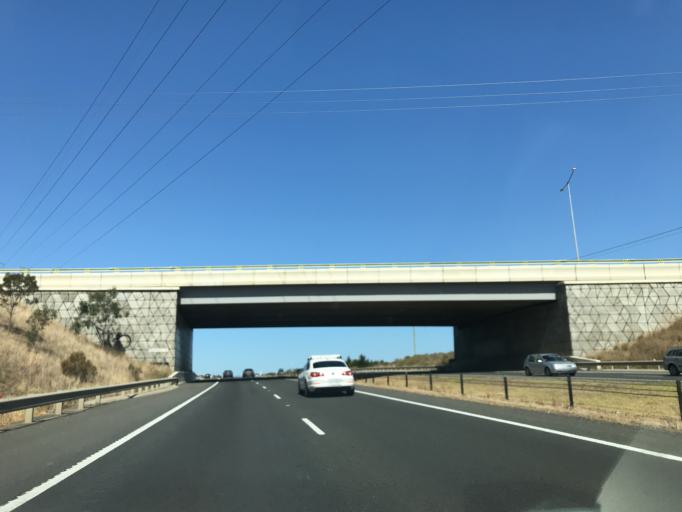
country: AU
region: Victoria
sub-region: Greater Geelong
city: Wandana Heights
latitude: -38.1710
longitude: 144.2921
